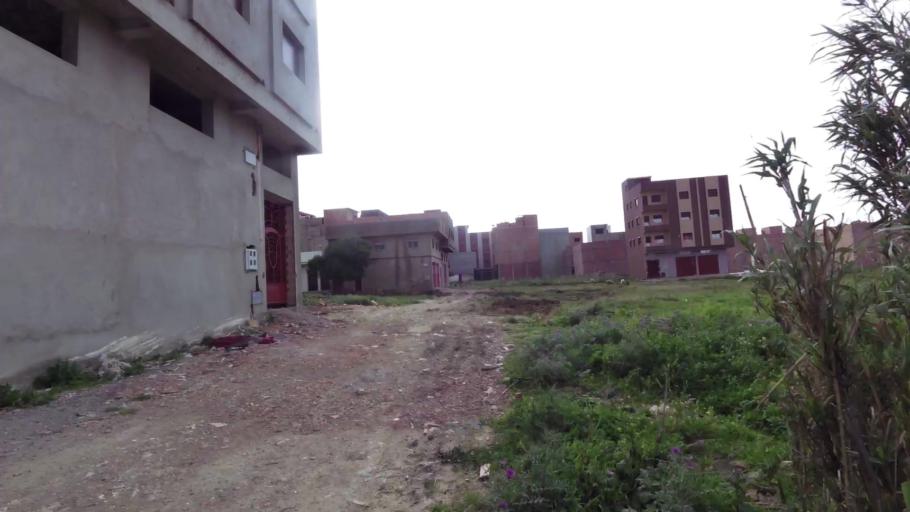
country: MA
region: Tanger-Tetouan
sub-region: Tanger-Assilah
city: Boukhalef
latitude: 35.7020
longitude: -5.9037
